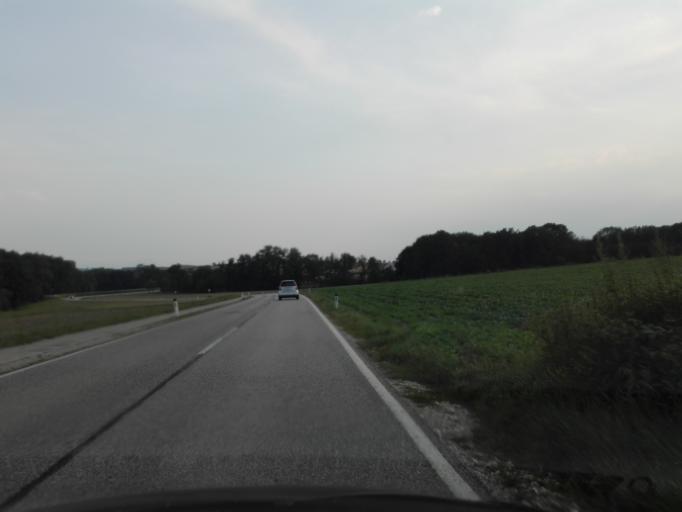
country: AT
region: Upper Austria
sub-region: Politischer Bezirk Grieskirchen
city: Grieskirchen
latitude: 48.2537
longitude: 13.8125
